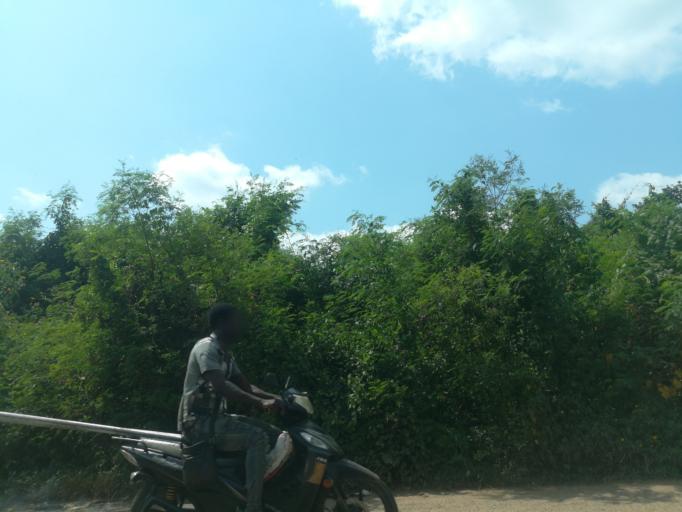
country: NG
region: Oyo
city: Moniya
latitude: 7.5698
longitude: 3.9104
